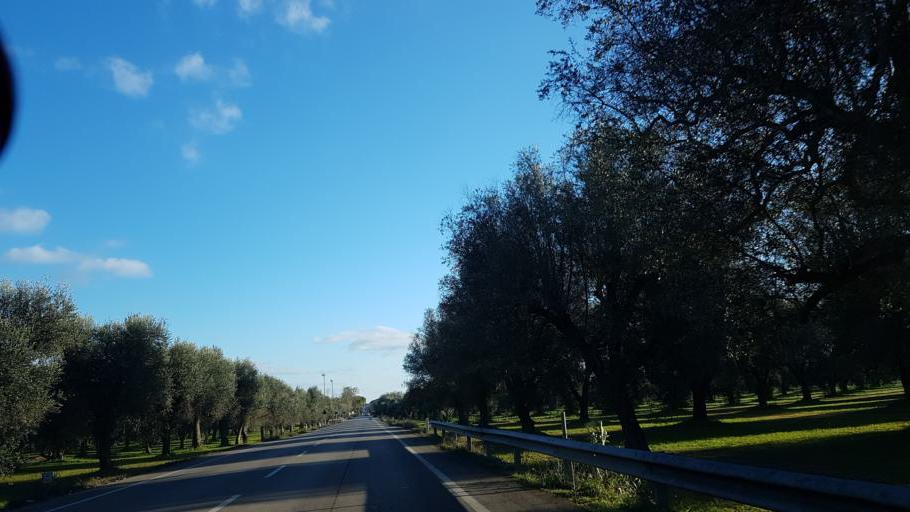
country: IT
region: Apulia
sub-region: Provincia di Lecce
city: Squinzano
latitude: 40.4485
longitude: 18.0301
